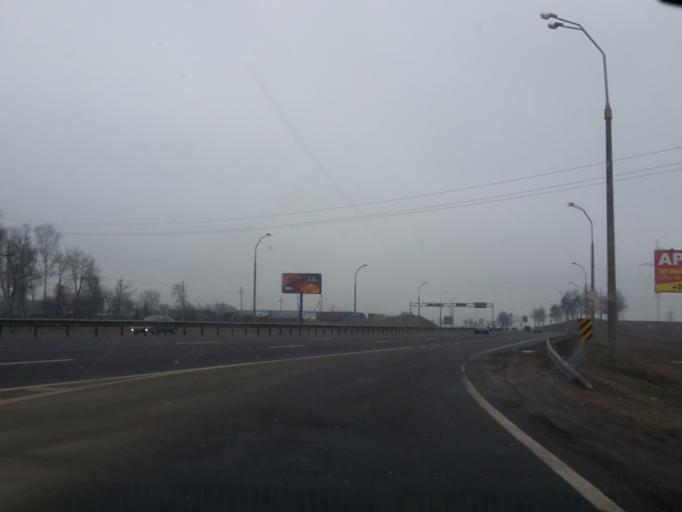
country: BY
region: Minsk
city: Zhdanovichy
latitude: 53.9092
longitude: 27.4086
